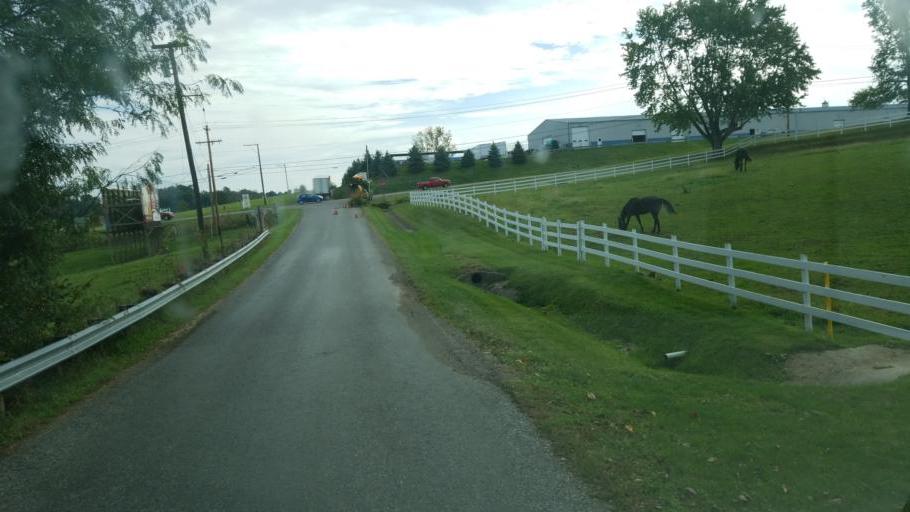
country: US
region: Ohio
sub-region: Holmes County
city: Millersburg
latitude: 40.5539
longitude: -81.8403
